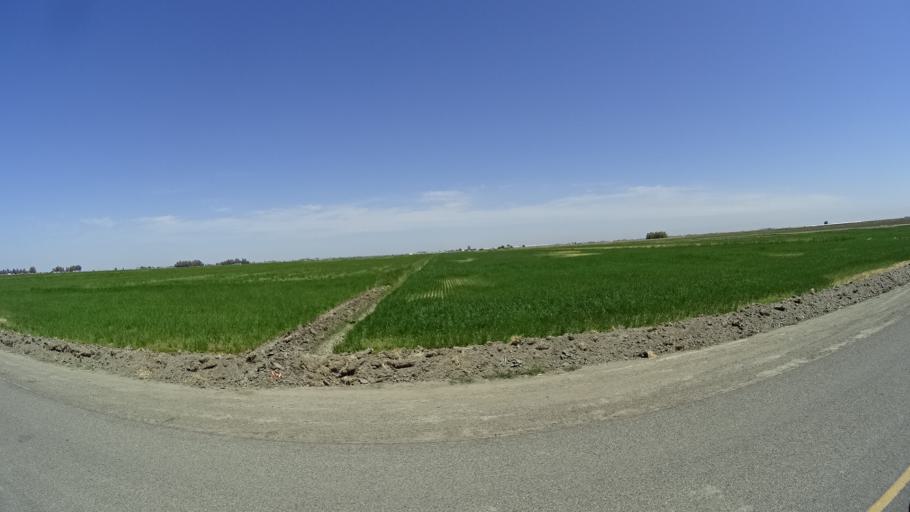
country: US
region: California
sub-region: Kings County
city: Stratford
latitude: 36.1893
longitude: -119.7641
